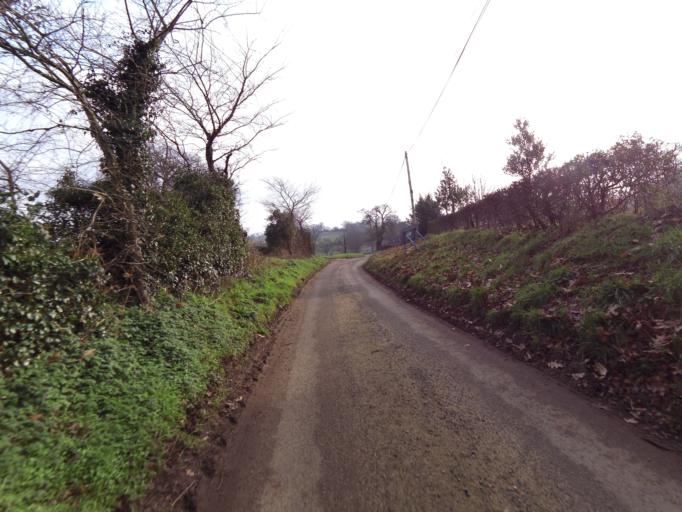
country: GB
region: England
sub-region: Suffolk
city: Woodbridge
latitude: 52.0662
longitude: 1.3060
